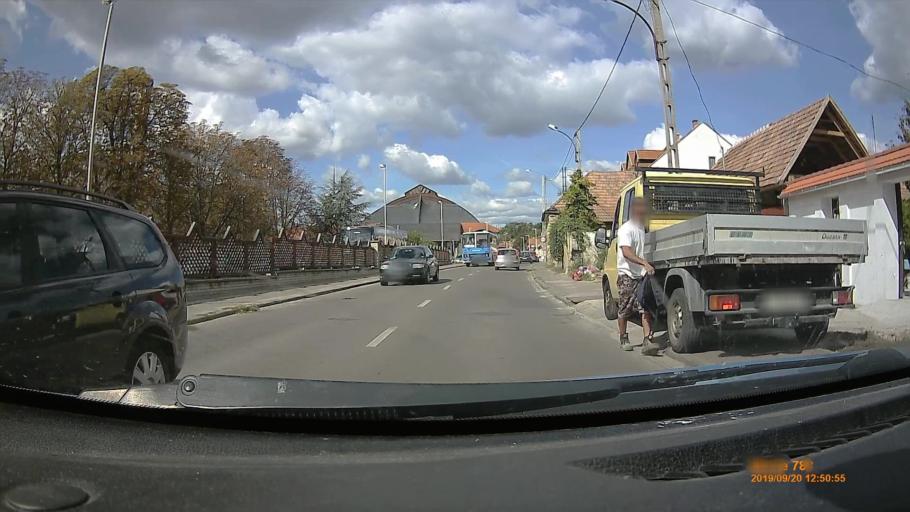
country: HU
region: Heves
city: Eger
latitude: 47.8981
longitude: 20.3853
